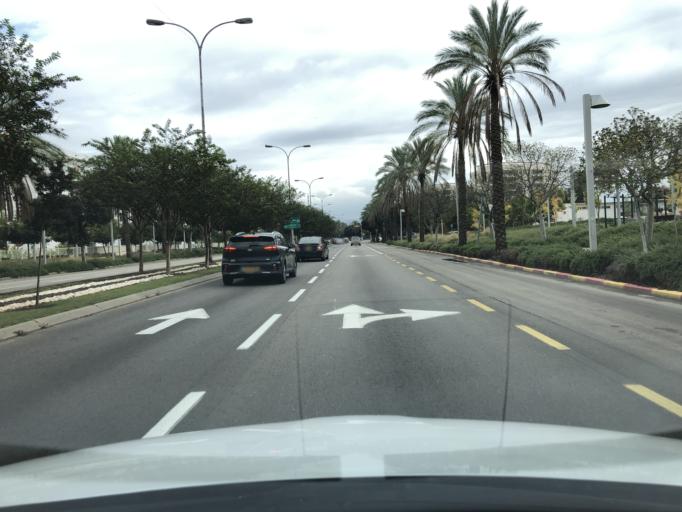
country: IL
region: Central District
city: Modiin
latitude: 31.9095
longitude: 35.0111
